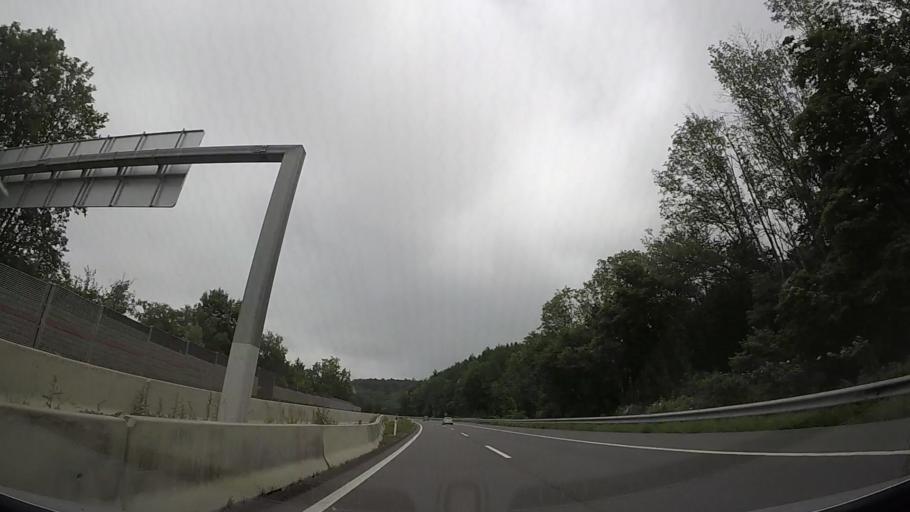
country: AT
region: Lower Austria
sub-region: Politischer Bezirk Sankt Polten
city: Eichgraben
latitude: 48.1537
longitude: 15.9855
